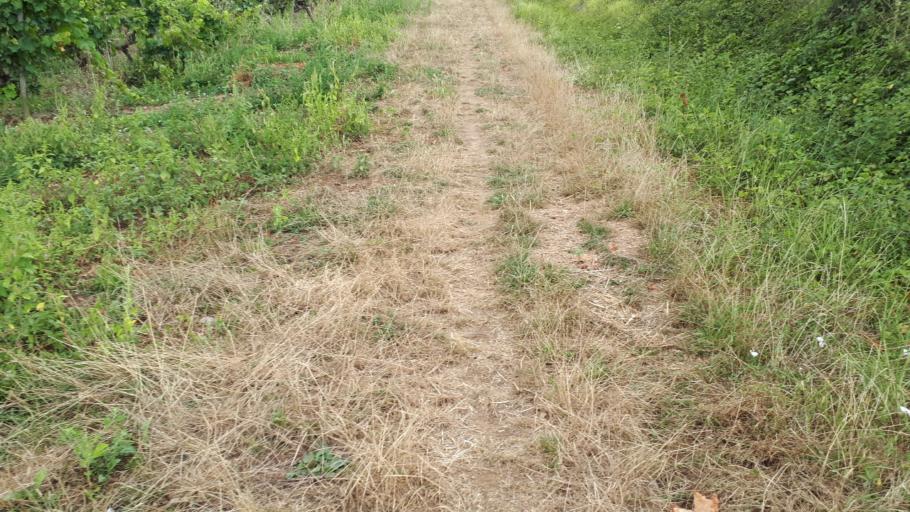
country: FR
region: Pays de la Loire
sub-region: Departement de Maine-et-Loire
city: Rochefort-sur-Loire
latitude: 47.3281
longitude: -0.6851
